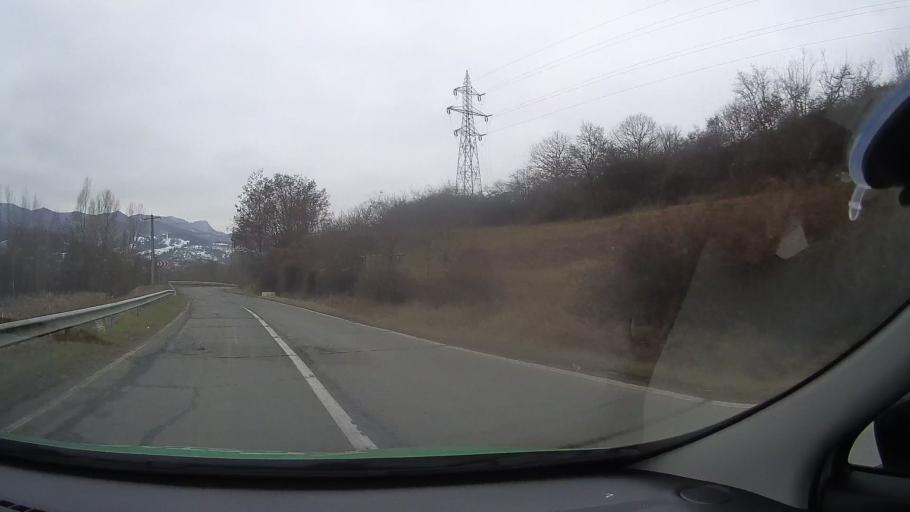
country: RO
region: Alba
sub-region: Comuna Ighiu
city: Ighiel
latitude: 46.1009
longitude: 23.4726
